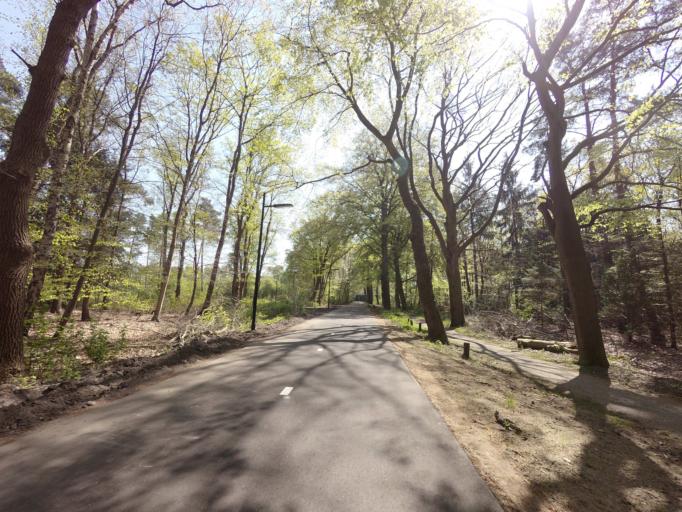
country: NL
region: Utrecht
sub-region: Gemeente Zeist
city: Zeist
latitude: 52.1116
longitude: 5.2736
